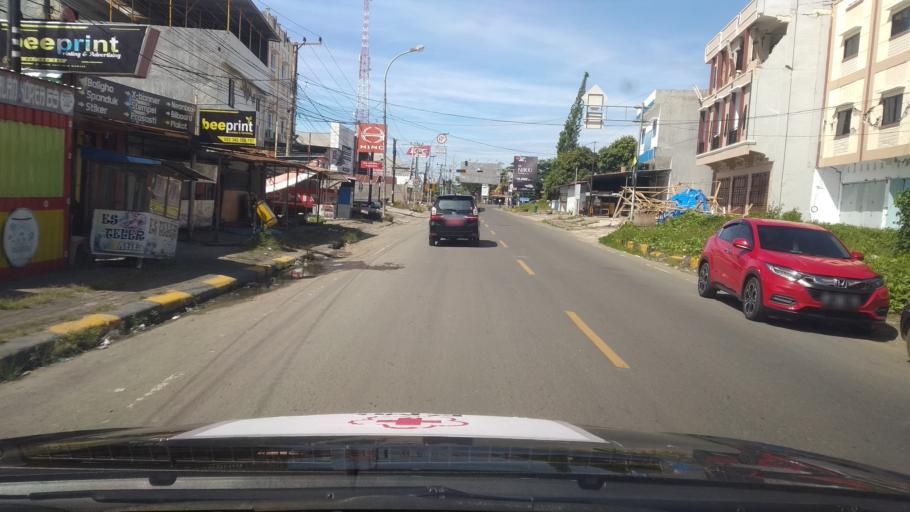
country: ID
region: Sulawesi Barat
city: Mamuju
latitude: -2.6840
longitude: 118.8698
